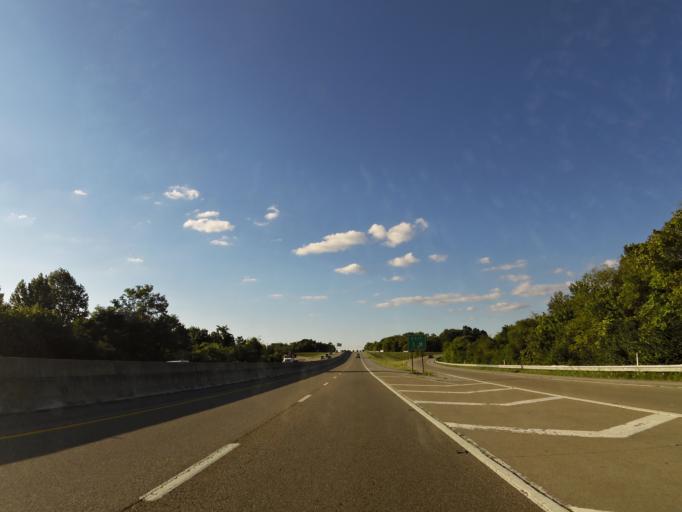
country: US
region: Tennessee
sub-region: Knox County
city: Farragut
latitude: 35.8976
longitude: -84.1168
